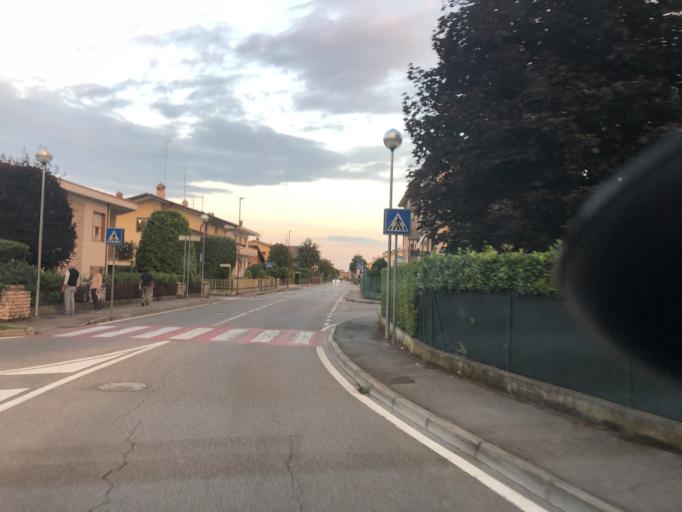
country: IT
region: Veneto
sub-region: Provincia di Verona
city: Bussolengo
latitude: 45.4649
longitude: 10.8534
